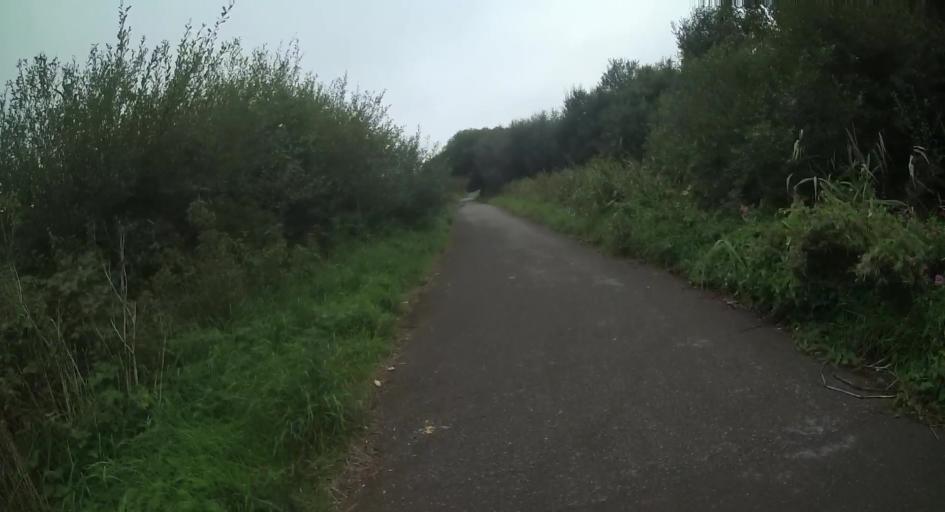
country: GB
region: England
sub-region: Isle of Wight
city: Newchurch
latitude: 50.6706
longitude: -1.1995
